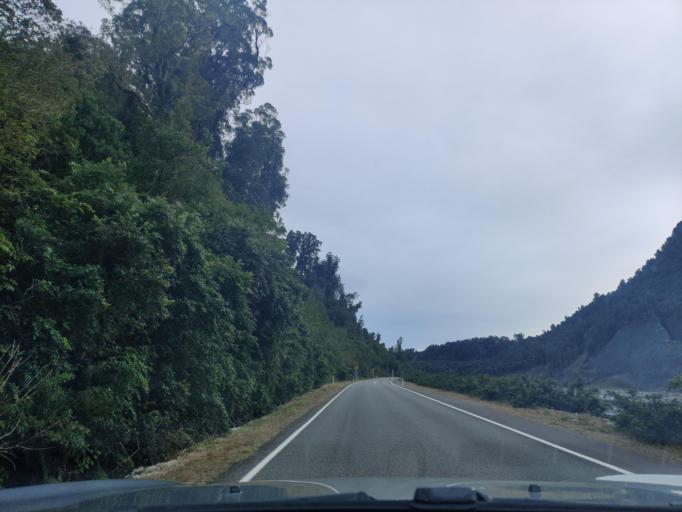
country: NZ
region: West Coast
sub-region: Westland District
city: Hokitika
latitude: -43.4013
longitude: 170.1798
